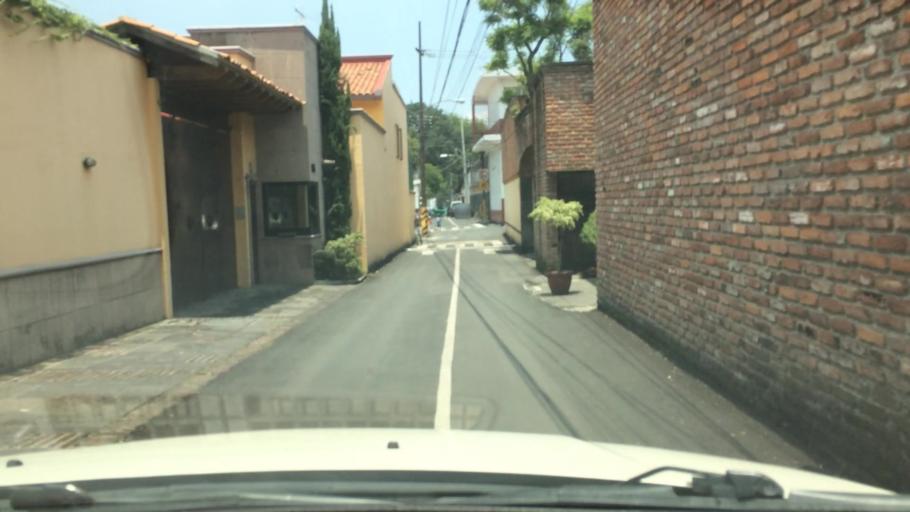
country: MX
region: Mexico City
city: Magdalena Contreras
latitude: 19.3259
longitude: -99.2255
